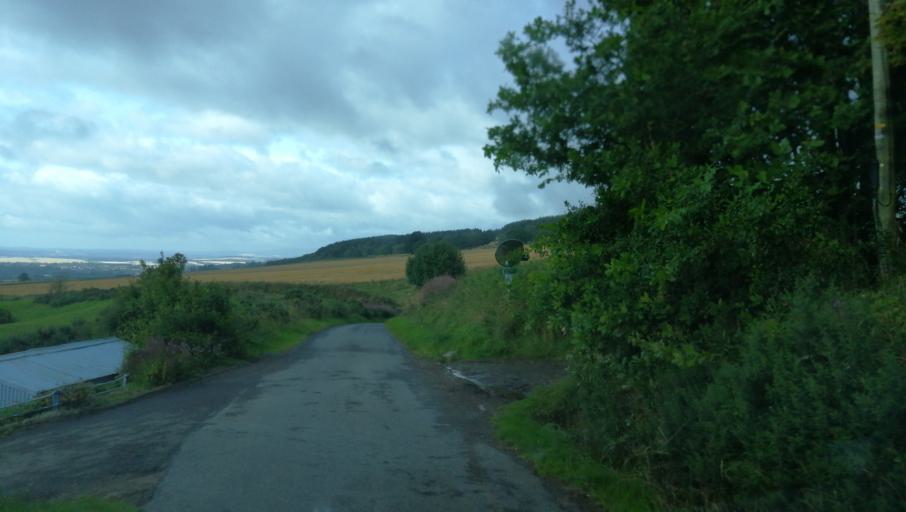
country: GB
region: Scotland
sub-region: Perth and Kinross
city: Alyth
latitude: 56.6172
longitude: -3.2861
